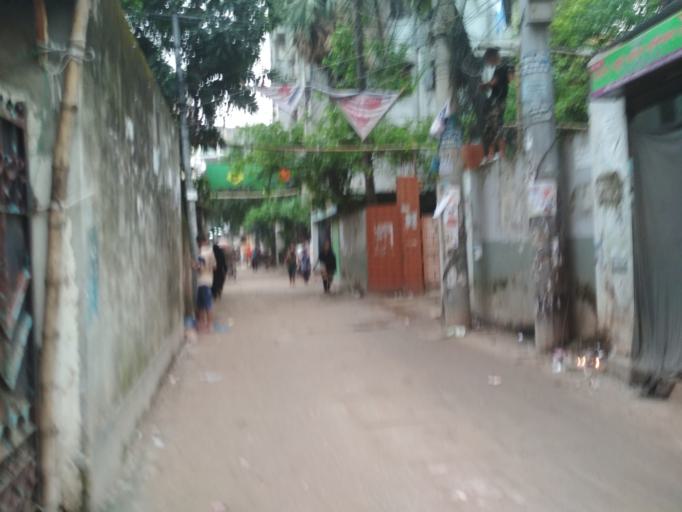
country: BD
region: Dhaka
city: Azimpur
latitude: 23.8030
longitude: 90.3649
